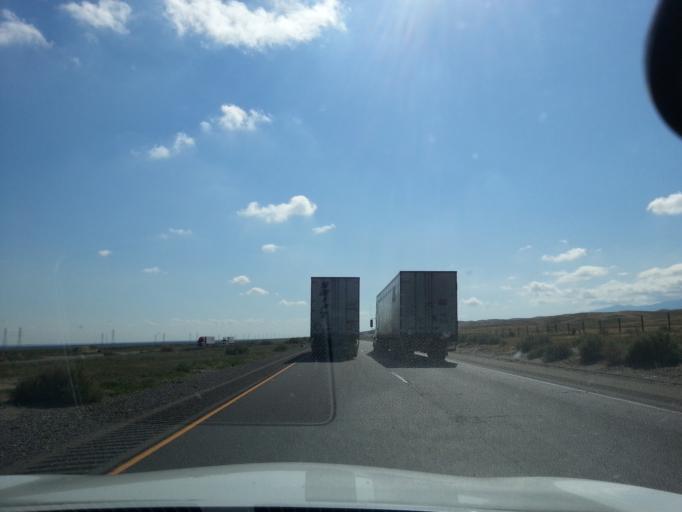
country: US
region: California
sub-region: Fresno County
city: Mendota
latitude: 36.5069
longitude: -120.4608
